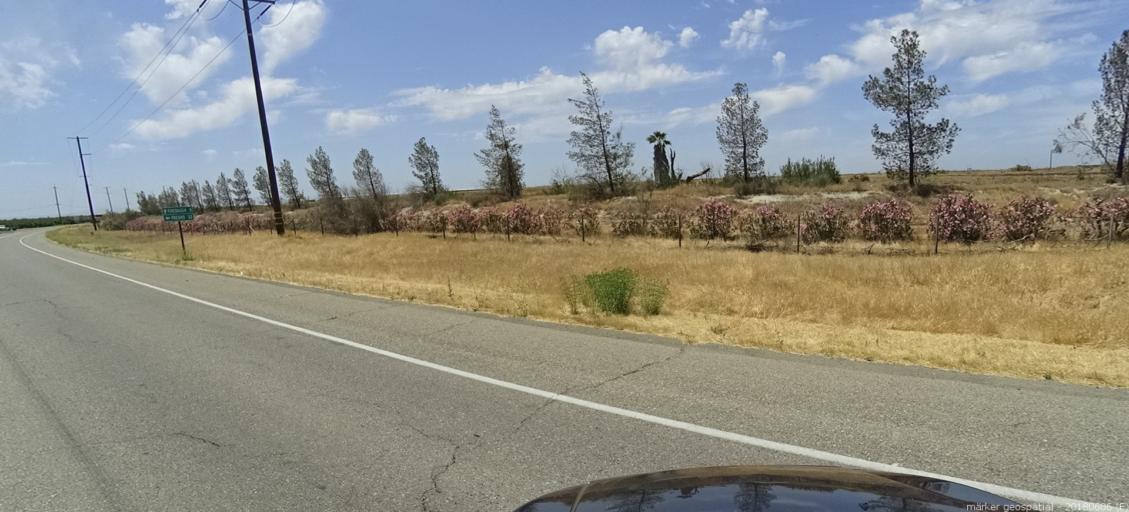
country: US
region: California
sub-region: Fresno County
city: Mendota
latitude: 36.8599
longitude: -120.3392
